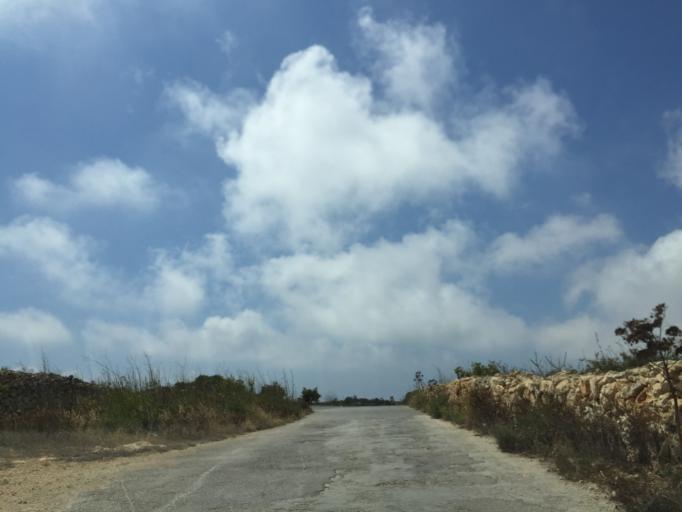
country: MT
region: Dingli
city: Dingli
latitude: 35.8607
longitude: 14.3730
